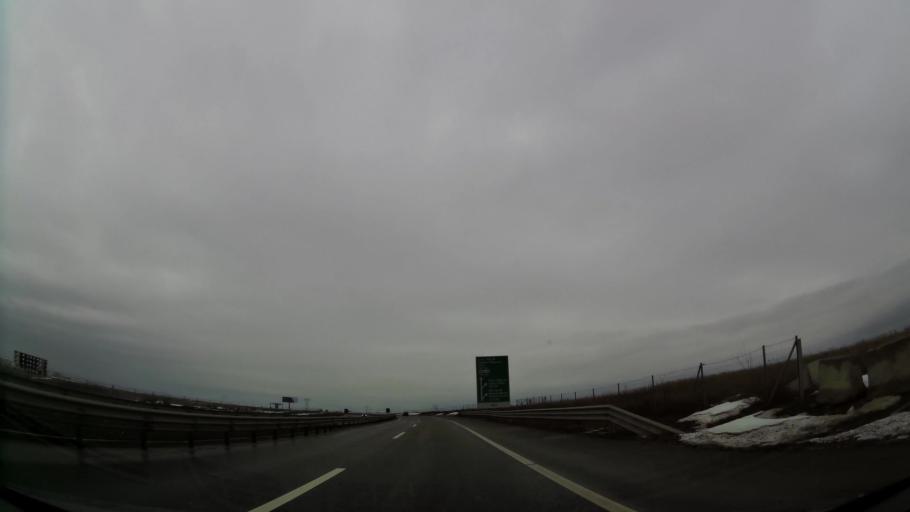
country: XK
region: Pristina
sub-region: Kosovo Polje
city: Kosovo Polje
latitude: 42.6257
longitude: 21.1306
